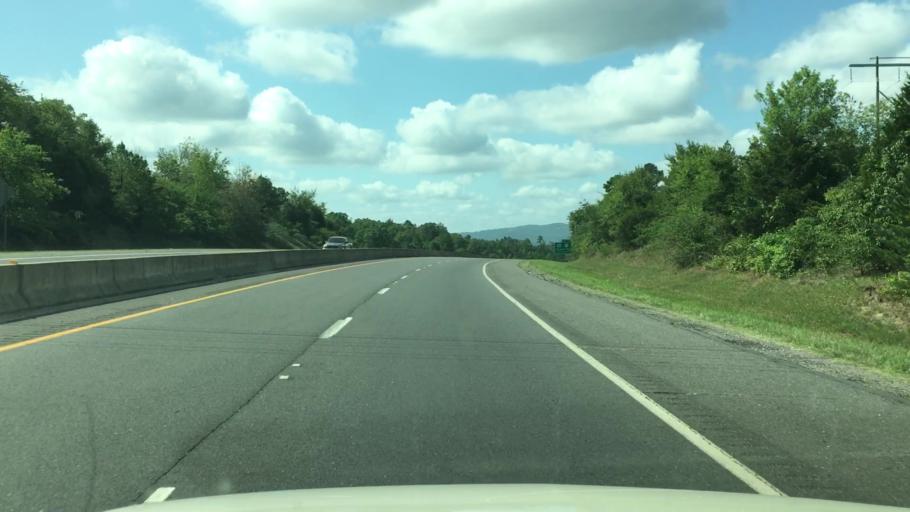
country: US
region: Arkansas
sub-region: Garland County
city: Piney
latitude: 34.4897
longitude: -93.1118
